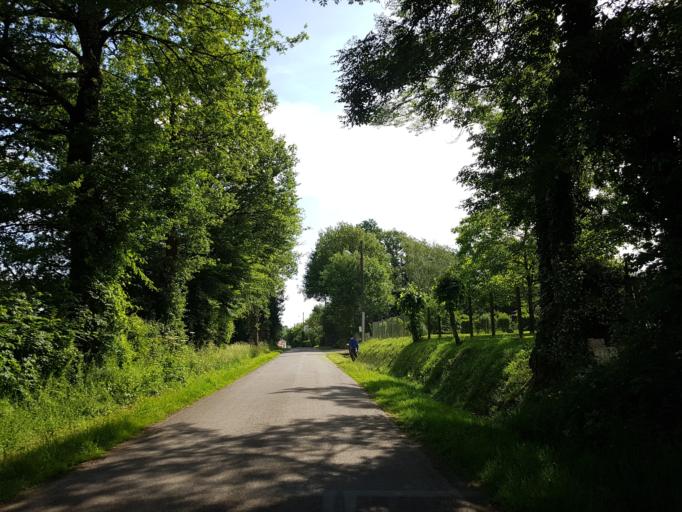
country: FR
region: Poitou-Charentes
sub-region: Departement de la Charente
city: Chabanais
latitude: 45.9200
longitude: 0.7085
